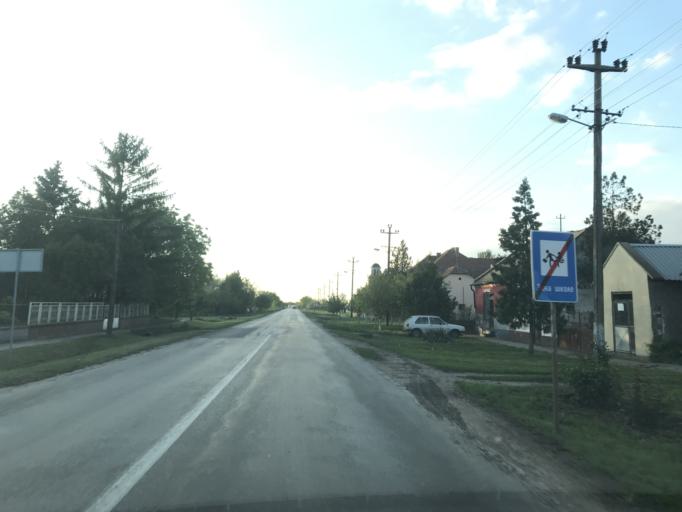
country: RS
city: Banatski Dvor
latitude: 45.5217
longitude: 20.5130
